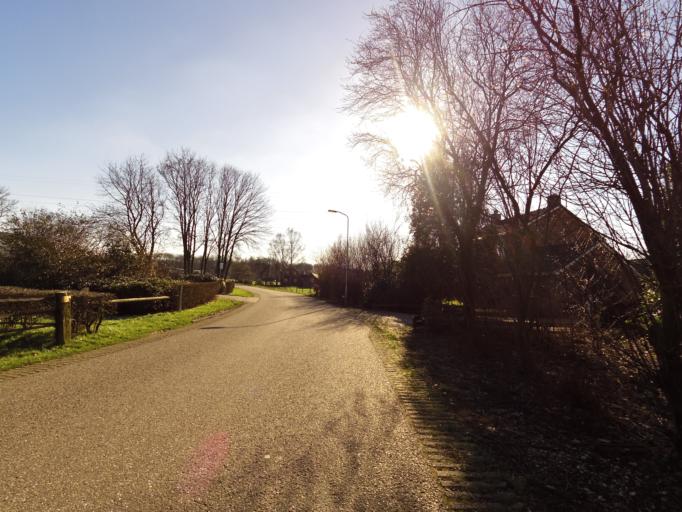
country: NL
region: Gelderland
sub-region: Gemeente Doesburg
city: Doesburg
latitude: 51.9377
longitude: 6.1607
